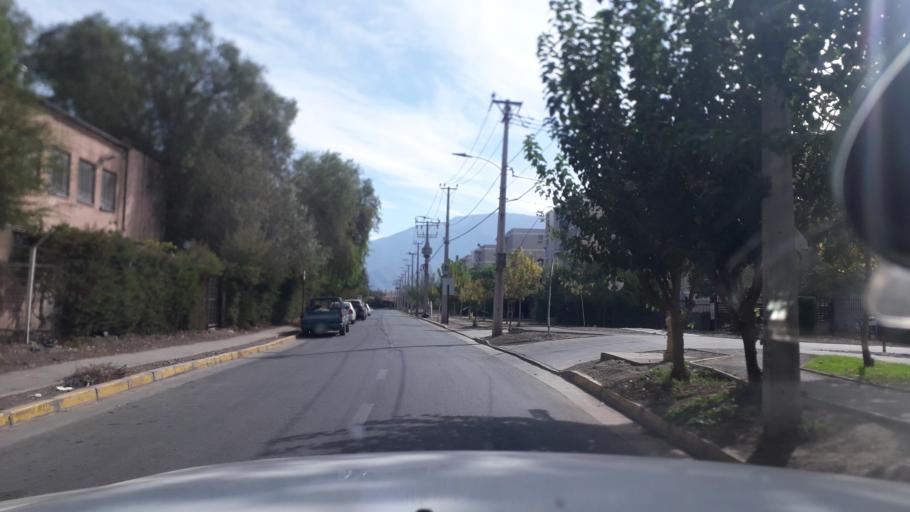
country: CL
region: Valparaiso
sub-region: Provincia de San Felipe
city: San Felipe
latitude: -32.7473
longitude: -70.7315
